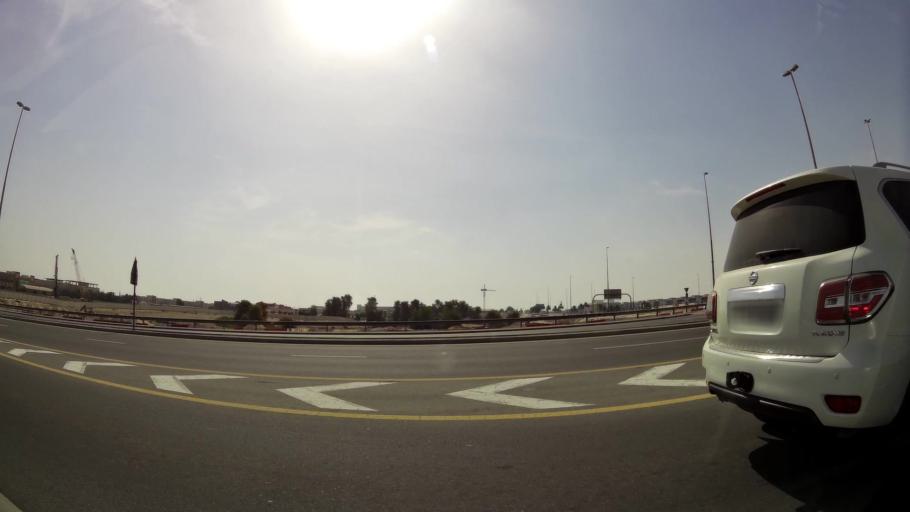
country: AE
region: Ash Shariqah
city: Sharjah
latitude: 25.2356
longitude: 55.4255
